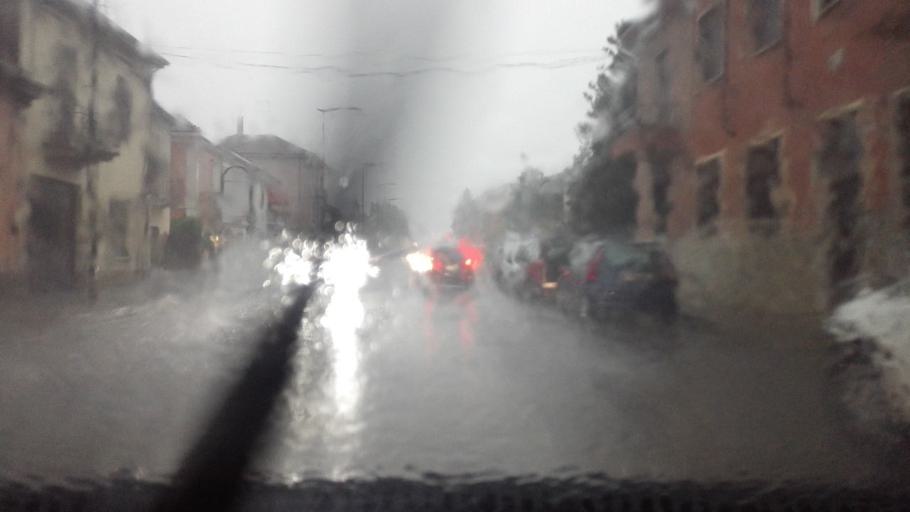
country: IT
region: Piedmont
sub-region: Provincia di Alessandria
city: Alessandria
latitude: 44.9185
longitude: 8.6059
